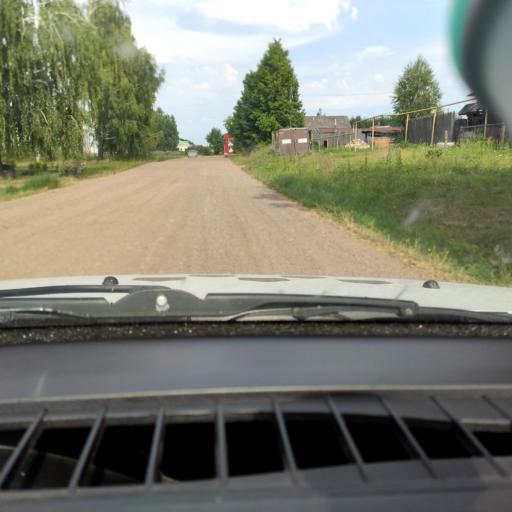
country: RU
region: Perm
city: Uinskoye
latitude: 57.1166
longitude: 56.5220
